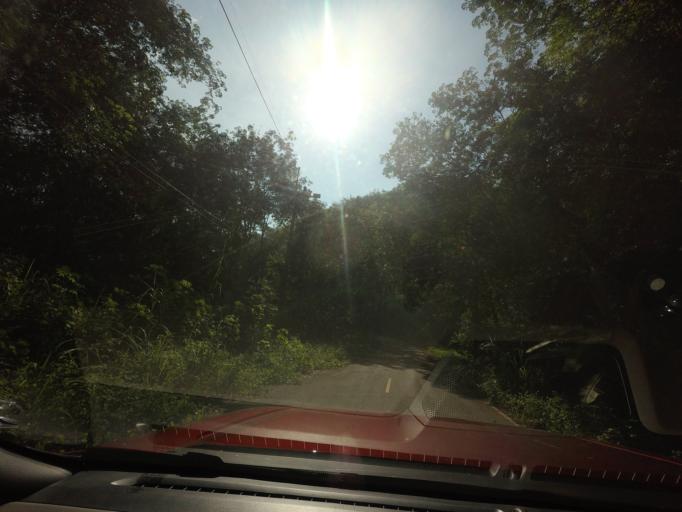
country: TH
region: Narathiwat
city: Si Sakhon
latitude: 6.0663
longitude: 101.3713
